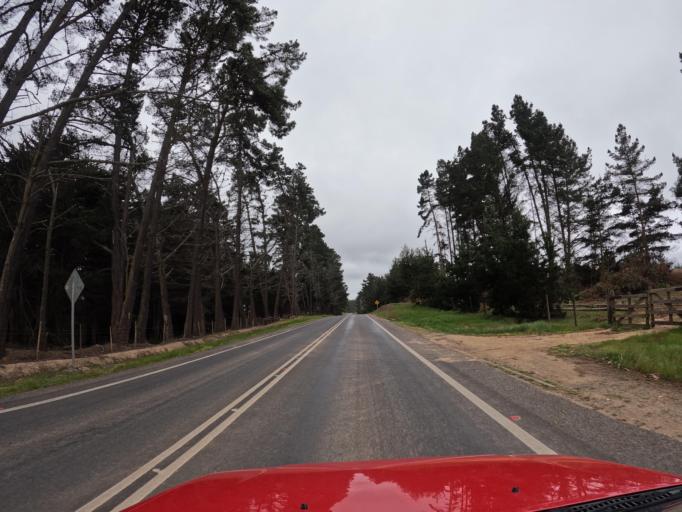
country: CL
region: O'Higgins
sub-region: Provincia de Colchagua
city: Santa Cruz
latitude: -34.5641
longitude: -72.0162
